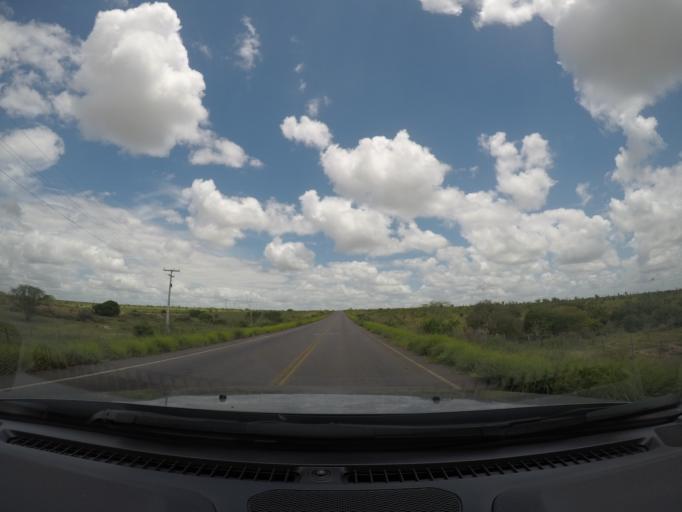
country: BR
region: Bahia
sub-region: Itaberaba
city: Itaberaba
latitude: -12.3551
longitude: -40.0302
